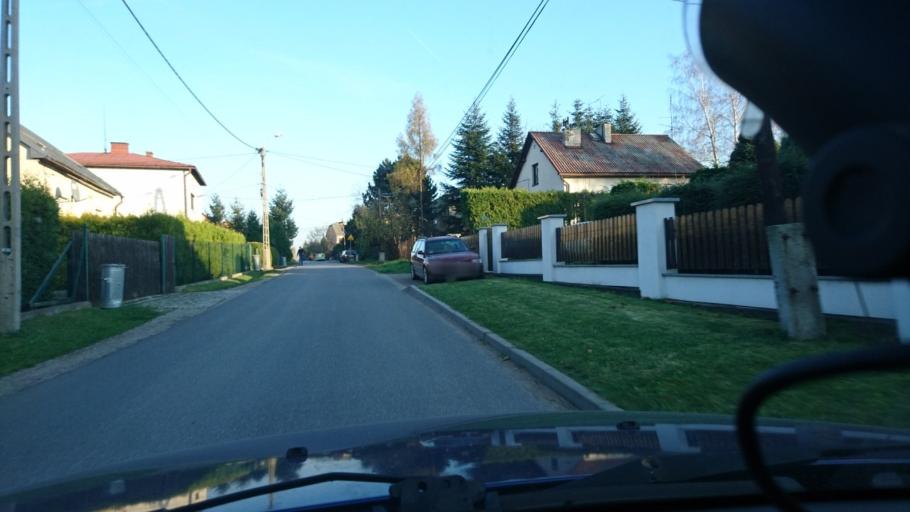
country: PL
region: Silesian Voivodeship
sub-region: Bielsko-Biala
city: Bielsko-Biala
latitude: 49.8610
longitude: 19.0293
